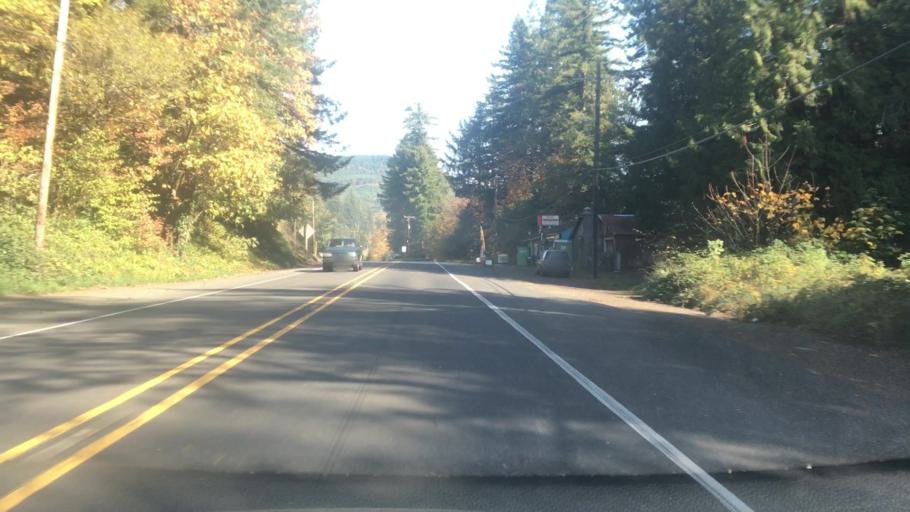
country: US
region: Oregon
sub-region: Lincoln County
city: Rose Lodge
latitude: 45.0194
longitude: -123.8660
